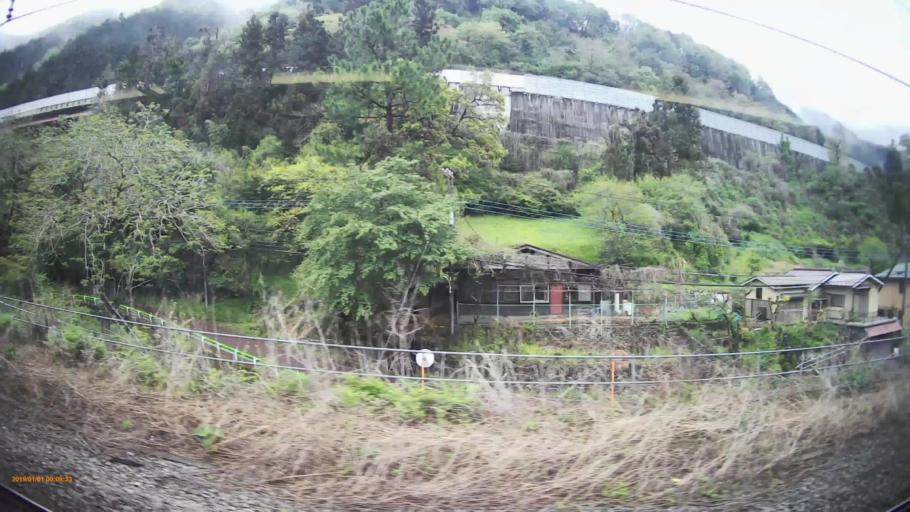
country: JP
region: Tokyo
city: Hachioji
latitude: 35.6392
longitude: 139.2385
